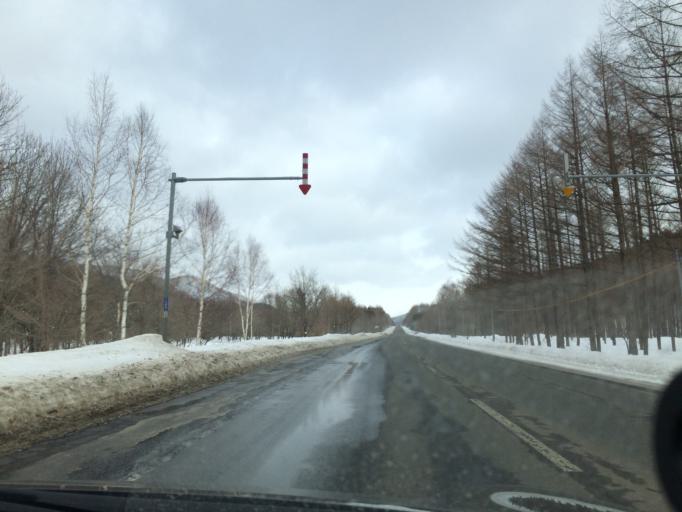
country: JP
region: Hokkaido
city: Shimo-furano
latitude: 43.1309
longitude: 142.6872
